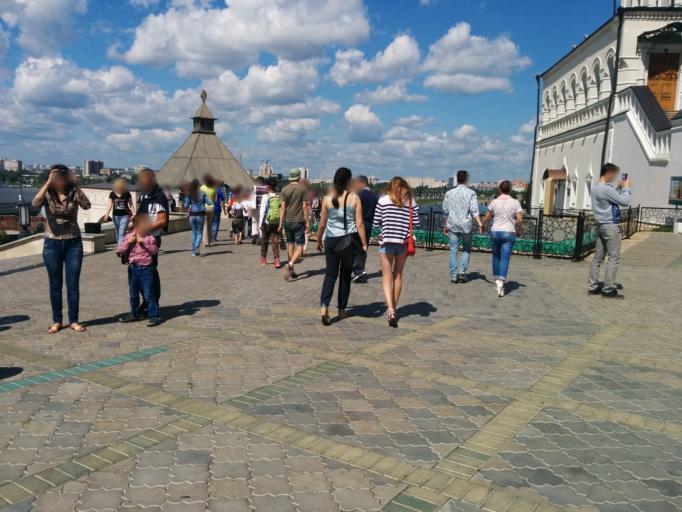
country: RU
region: Tatarstan
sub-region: Gorod Kazan'
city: Kazan
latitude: 55.8004
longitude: 49.1050
